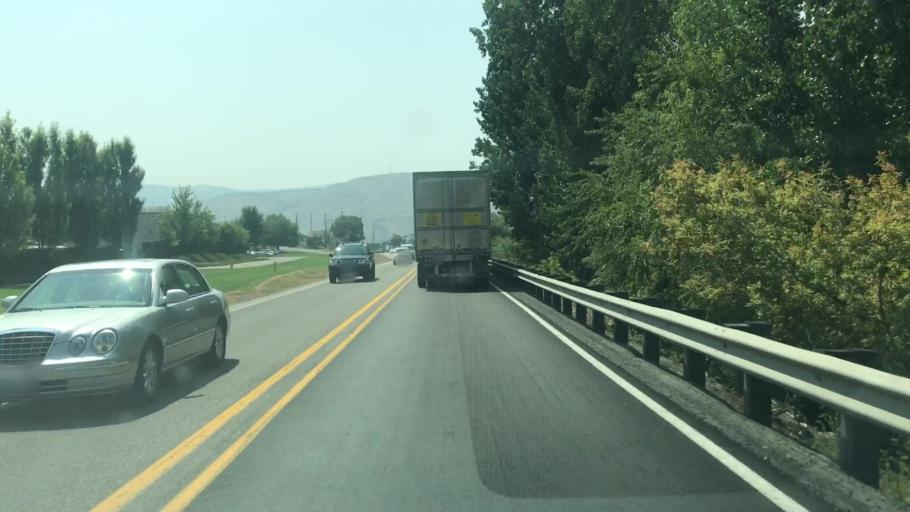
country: US
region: Washington
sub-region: Douglas County
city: East Wenatchee
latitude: 47.4239
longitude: -120.2977
